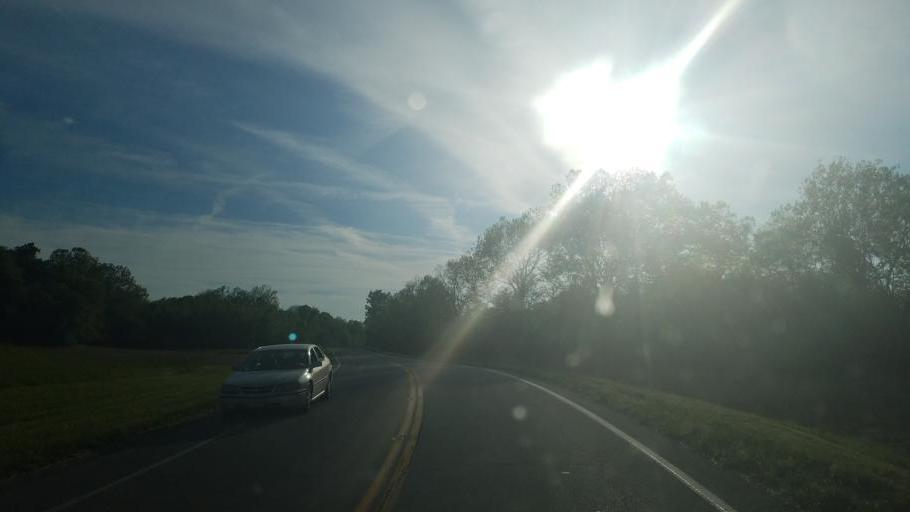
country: US
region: Ohio
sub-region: Ross County
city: Frankfort
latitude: 39.4282
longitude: -83.2307
